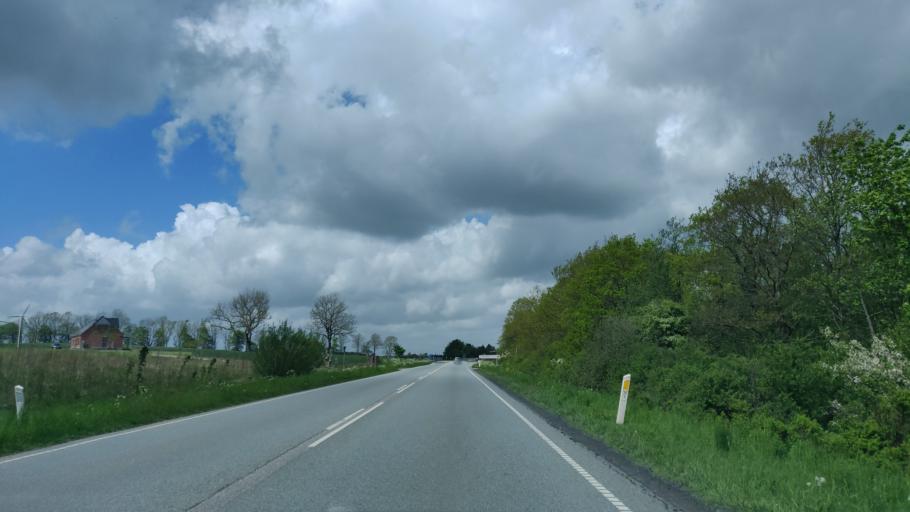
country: DK
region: Central Jutland
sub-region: Hedensted Kommune
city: Torring
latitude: 55.8414
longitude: 9.5016
